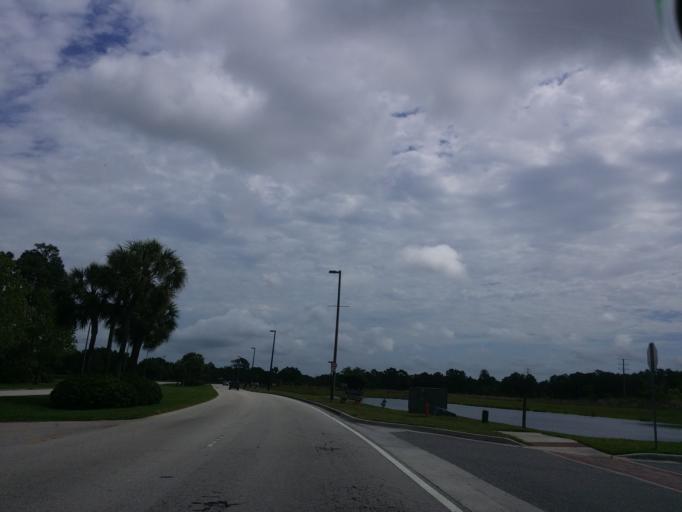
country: US
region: Florida
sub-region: Orange County
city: Williamsburg
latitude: 28.3948
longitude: -81.4647
